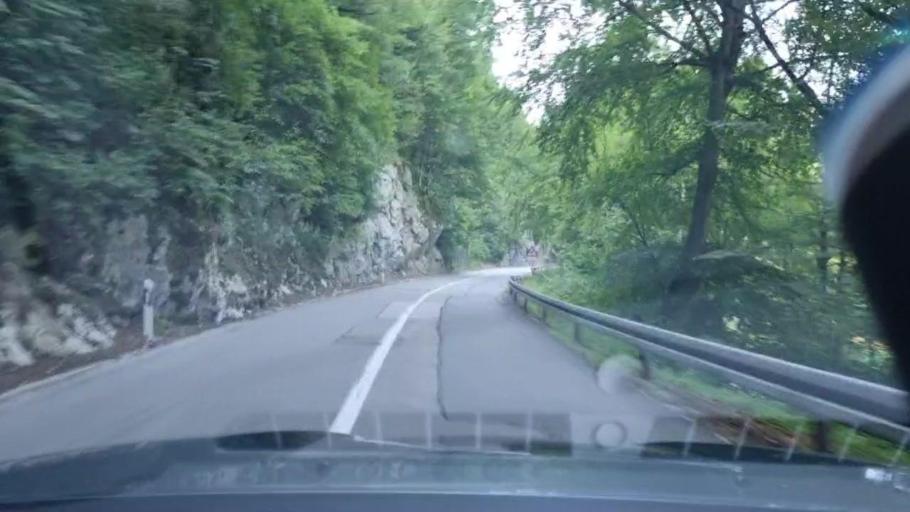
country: BA
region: Federation of Bosnia and Herzegovina
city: Stijena
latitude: 44.8921
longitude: 16.0490
